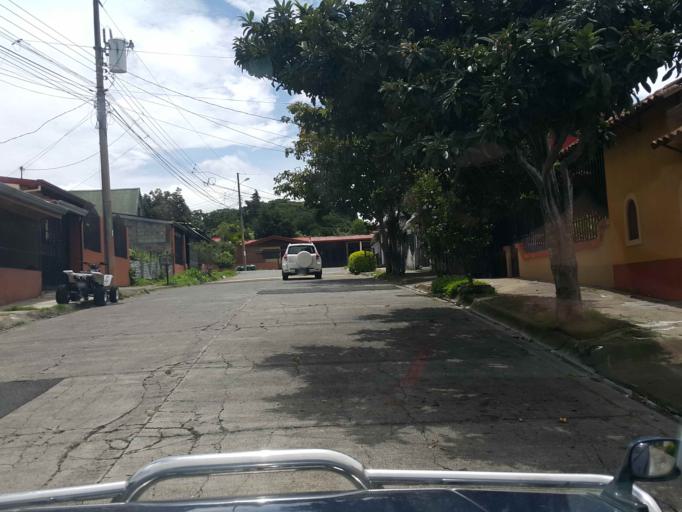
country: CR
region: Heredia
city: Heredia
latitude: 10.0182
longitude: -84.1169
